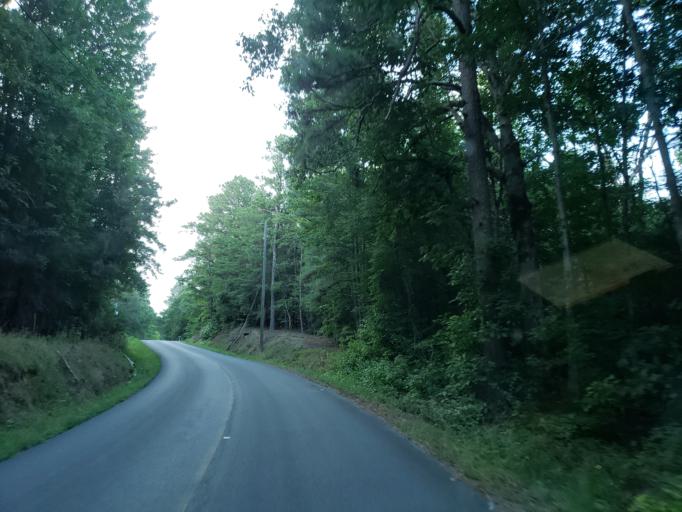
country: US
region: Georgia
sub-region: Bartow County
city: Euharlee
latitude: 34.0771
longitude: -84.9435
